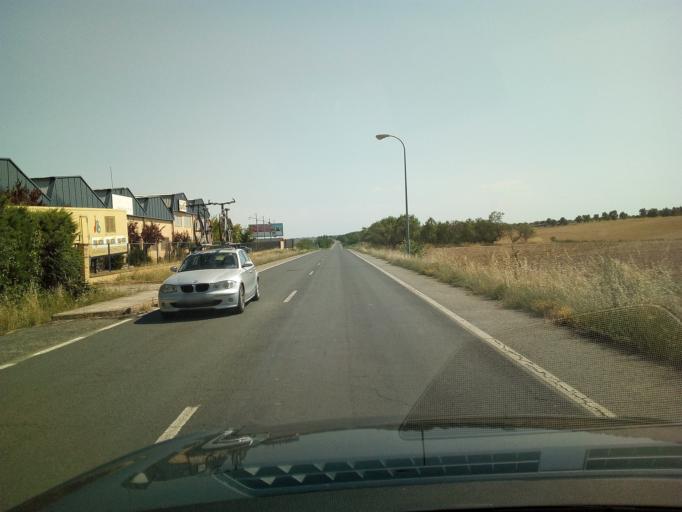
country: ES
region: Navarre
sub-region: Provincia de Navarra
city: Olite
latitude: 42.4749
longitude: -1.6493
